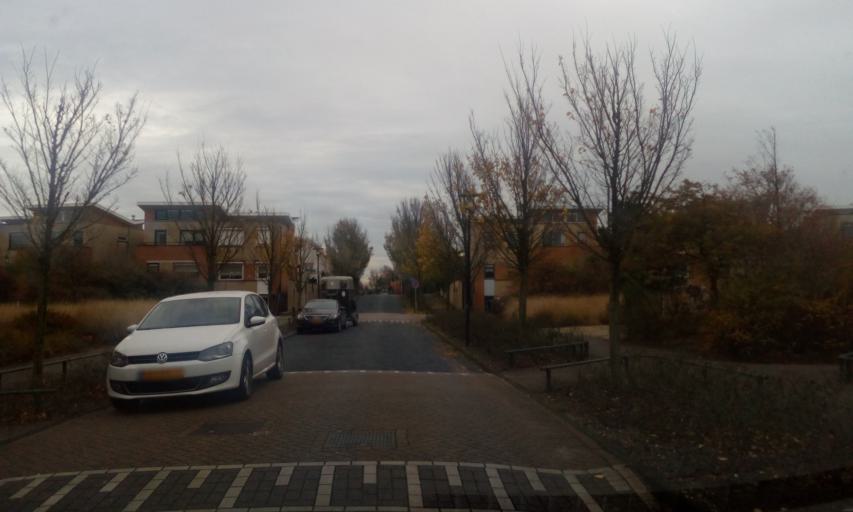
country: NL
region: South Holland
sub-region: Gemeente Westland
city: Monster
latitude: 52.0223
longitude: 4.1655
